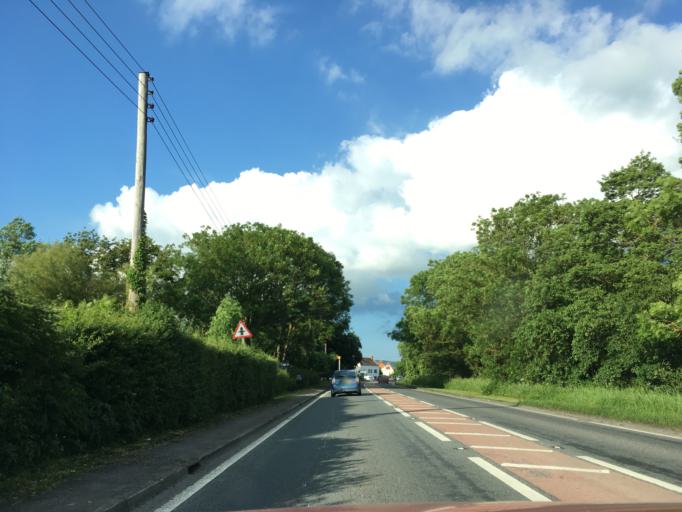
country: GB
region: England
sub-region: North Somerset
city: Bleadon
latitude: 51.2657
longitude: -2.9098
